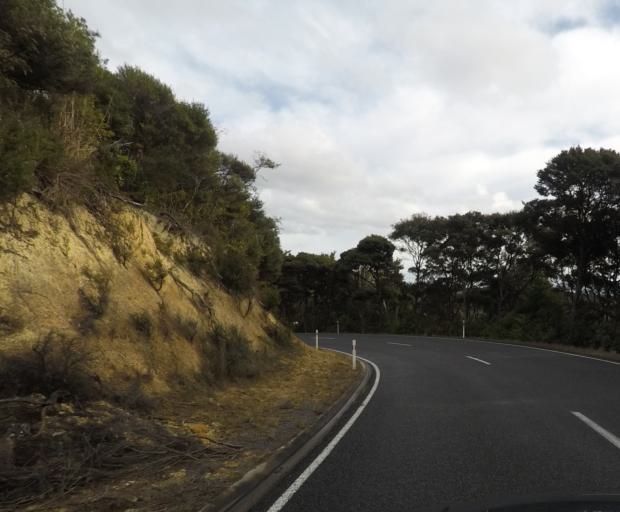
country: NZ
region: Northland
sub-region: Whangarei
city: Ruakaka
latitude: -36.0592
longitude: 174.5632
